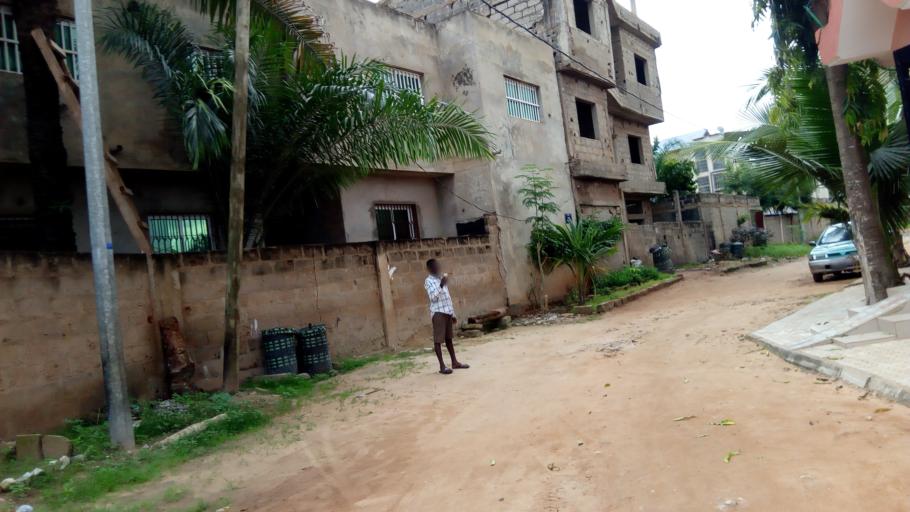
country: TG
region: Maritime
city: Lome
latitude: 6.1713
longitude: 1.1878
